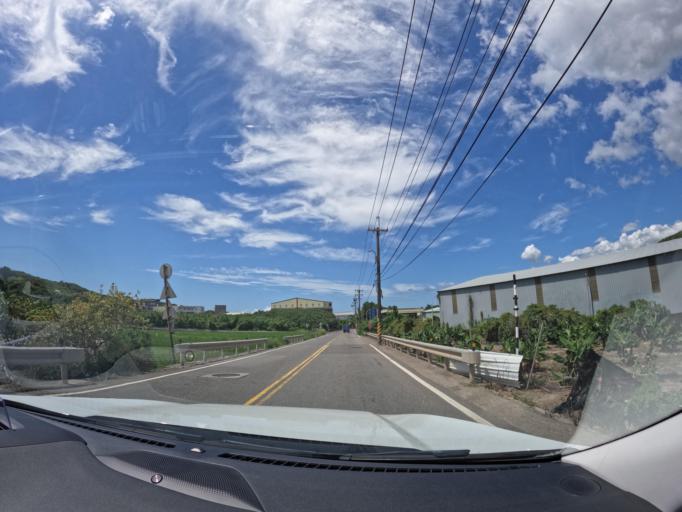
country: TW
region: Taipei
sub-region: Taipei
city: Banqiao
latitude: 25.1262
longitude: 121.3909
